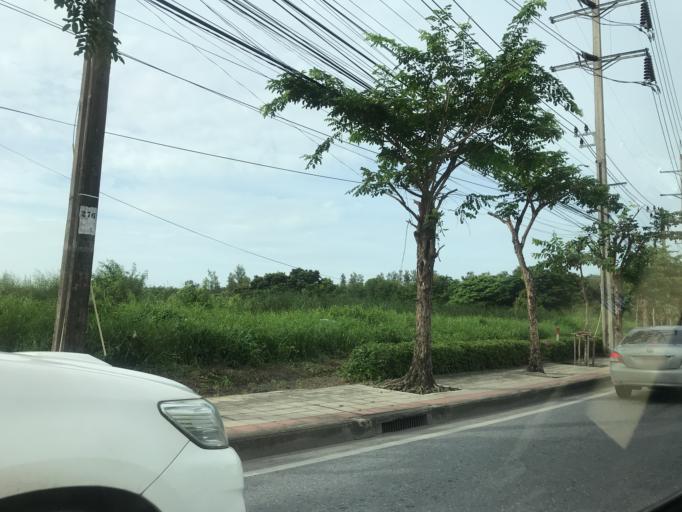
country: TH
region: Bangkok
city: Bueng Kum
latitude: 13.7898
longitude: 100.6789
